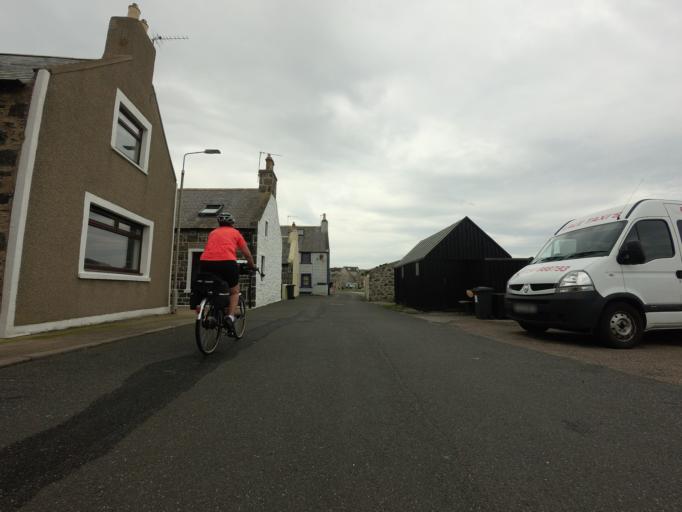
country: GB
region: Scotland
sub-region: Aberdeenshire
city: Whitehills
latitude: 57.6776
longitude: -2.5824
